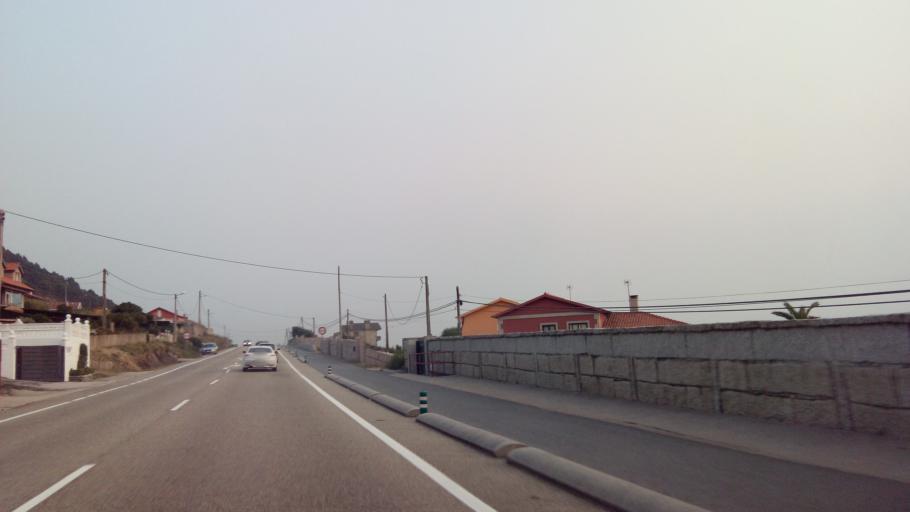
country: ES
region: Galicia
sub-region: Provincia de Pontevedra
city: Baiona
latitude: 42.0982
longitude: -8.8938
